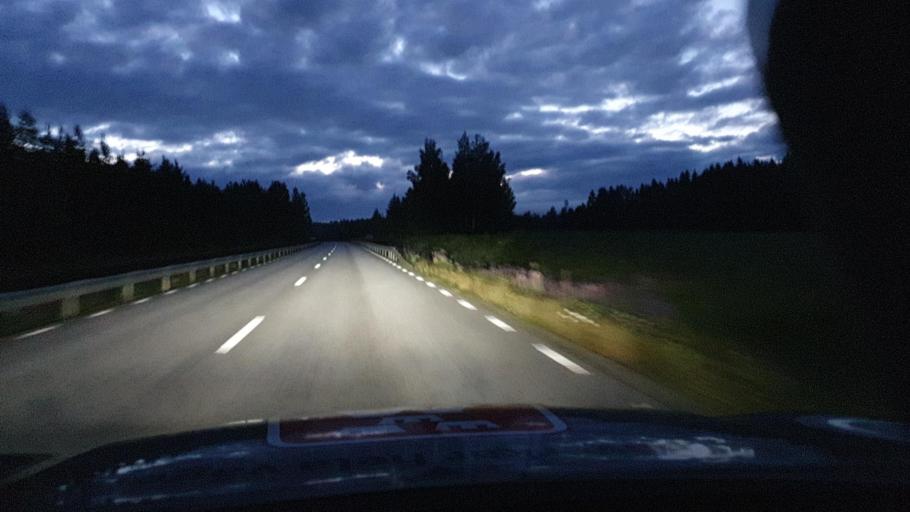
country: SE
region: OErebro
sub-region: Karlskoga Kommun
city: Karlskoga
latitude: 59.4279
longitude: 14.5149
